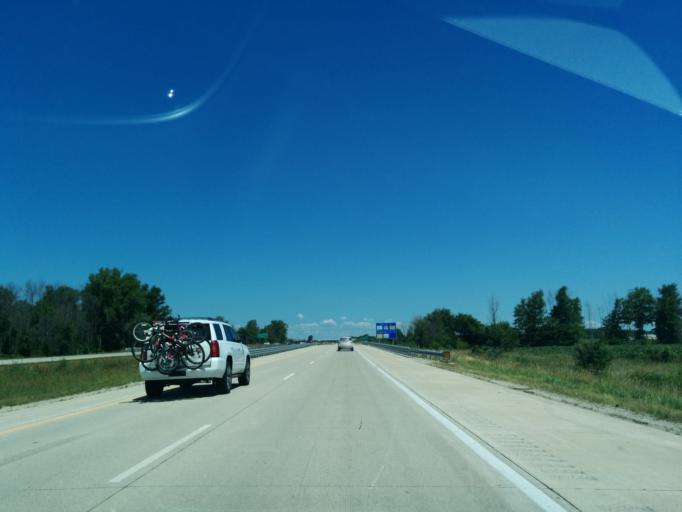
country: US
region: Michigan
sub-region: Bay County
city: Pinconning
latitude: 43.8429
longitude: -84.0204
